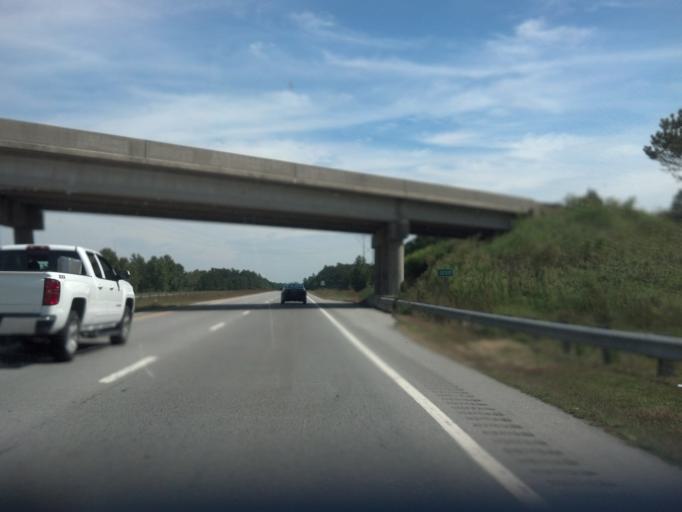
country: US
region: North Carolina
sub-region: Pitt County
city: Farmville
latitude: 35.6027
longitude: -77.5259
